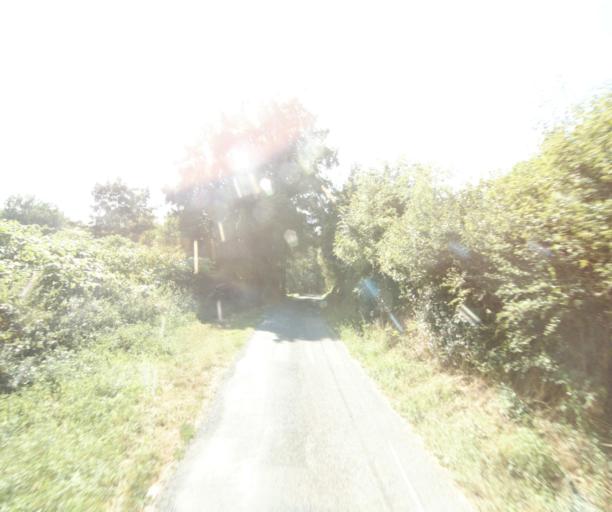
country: FR
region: Rhone-Alpes
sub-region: Departement du Rhone
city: Bessenay
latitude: 45.7729
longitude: 4.5759
